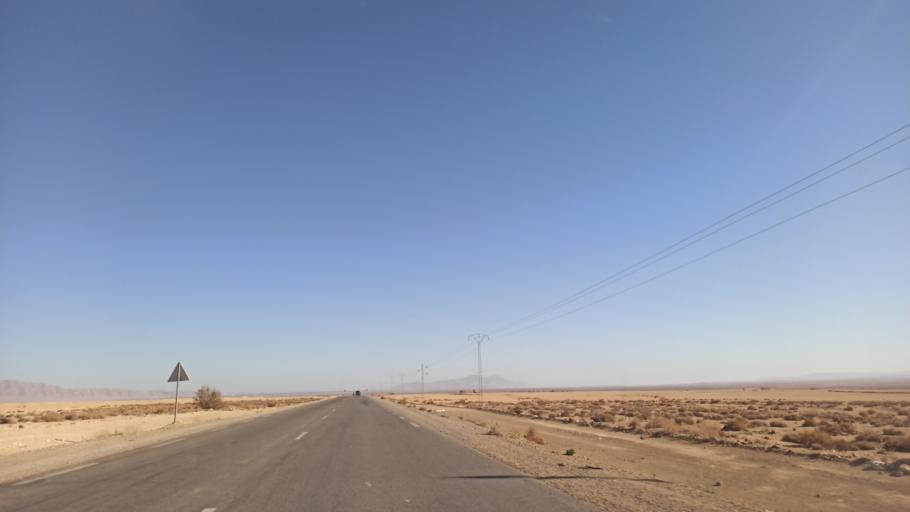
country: TN
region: Gafsa
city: Al Metlaoui
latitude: 34.3237
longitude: 8.5306
